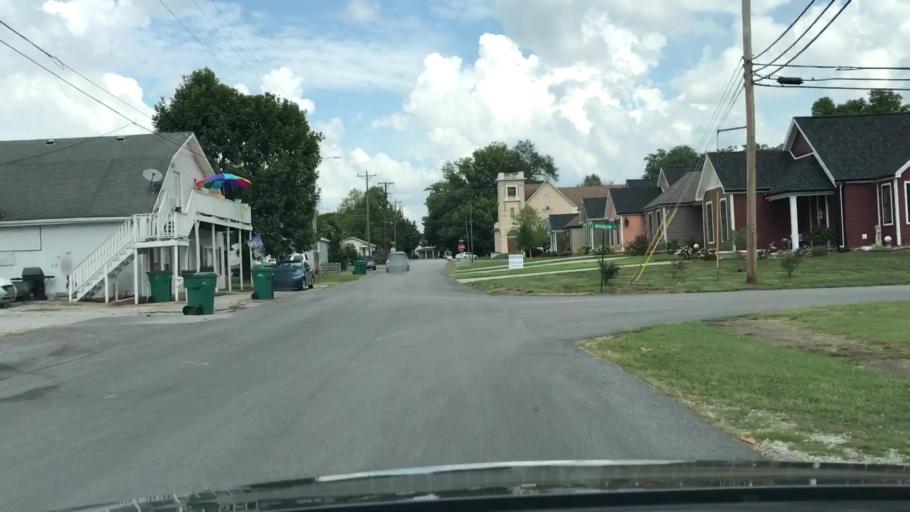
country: US
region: Kentucky
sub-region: Todd County
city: Elkton
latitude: 36.8079
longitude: -87.1505
